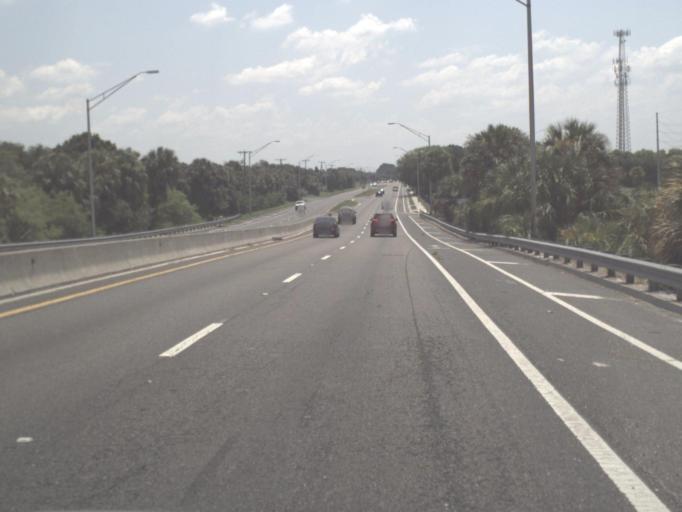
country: US
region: Florida
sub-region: Hillsborough County
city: Gibsonton
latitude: 27.8579
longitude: -82.3834
